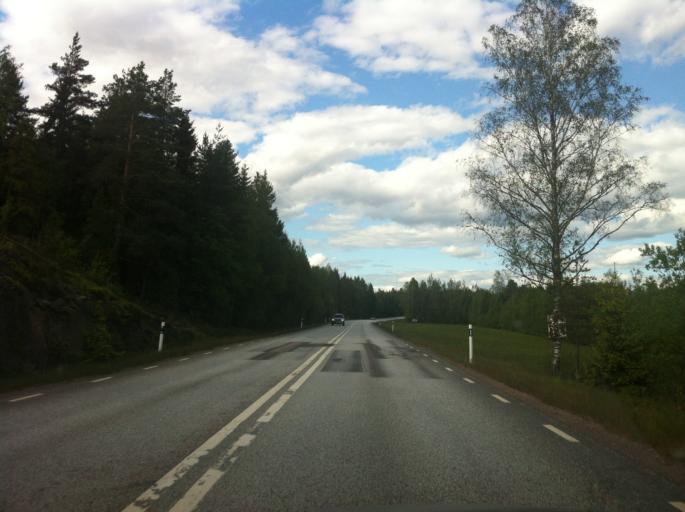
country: SE
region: Vaermland
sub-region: Storfors Kommun
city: Storfors
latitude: 59.5155
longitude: 14.2688
